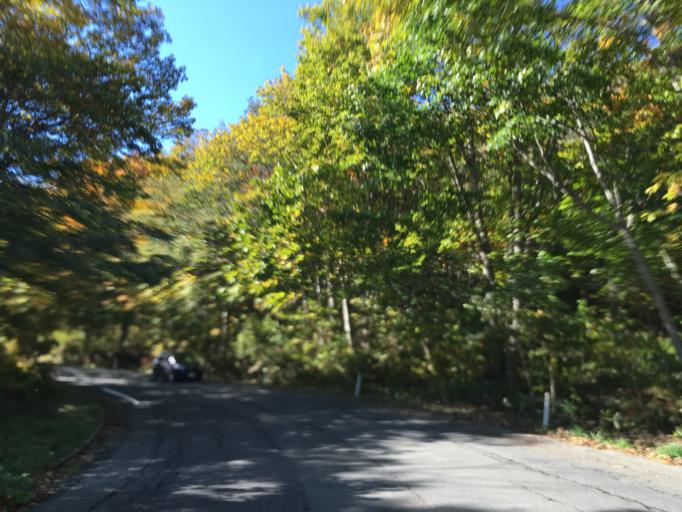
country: JP
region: Fukushima
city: Inawashiro
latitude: 37.5944
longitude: 140.2465
